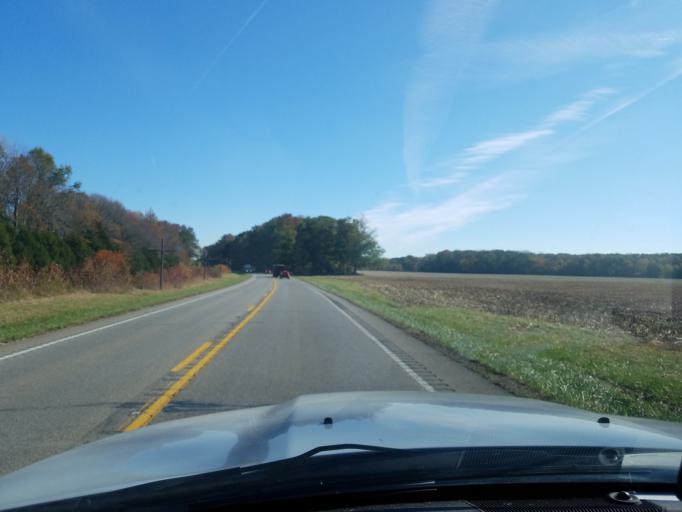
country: US
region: Indiana
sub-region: Jennings County
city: Country Squire Lakes
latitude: 38.9804
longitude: -85.6973
